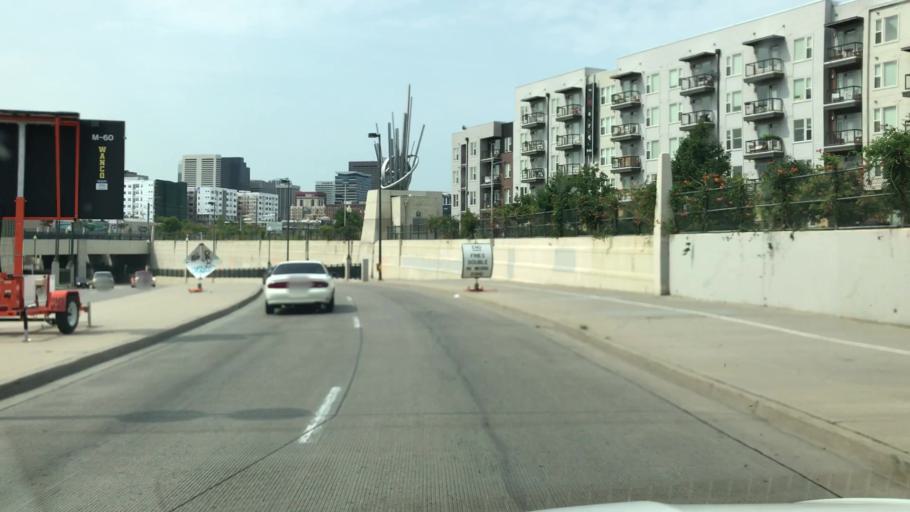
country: US
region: Colorado
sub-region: Denver County
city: Denver
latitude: 39.7633
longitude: -104.9879
